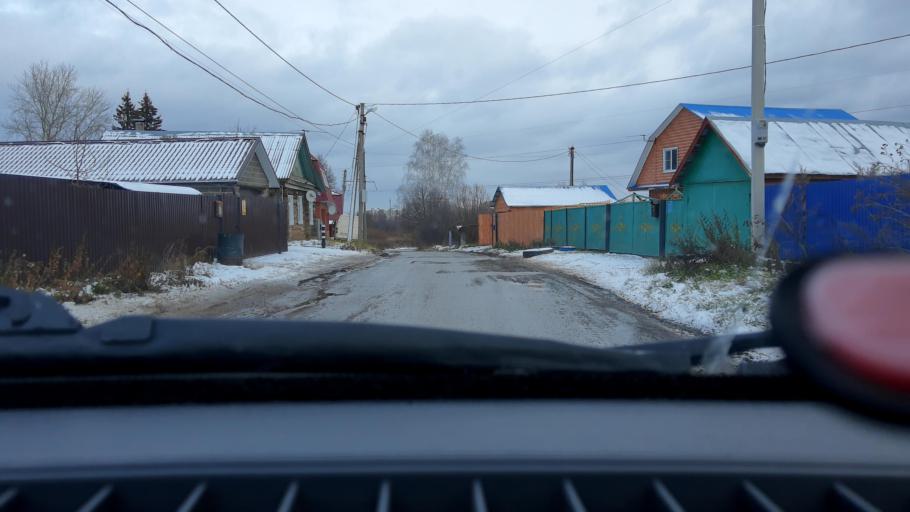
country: RU
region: Bashkortostan
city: Avdon
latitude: 54.7046
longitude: 55.7922
